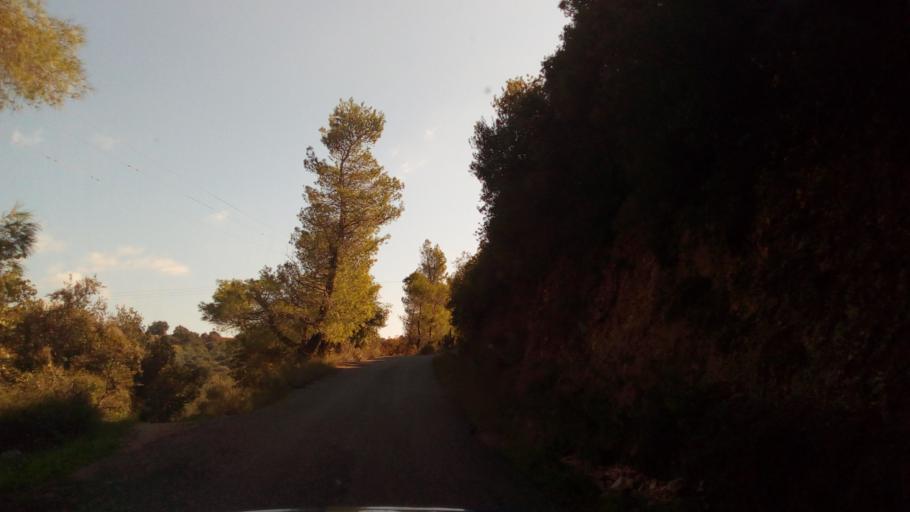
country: GR
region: West Greece
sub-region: Nomos Aitolias kai Akarnanias
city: Nafpaktos
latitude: 38.4190
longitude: 21.8451
